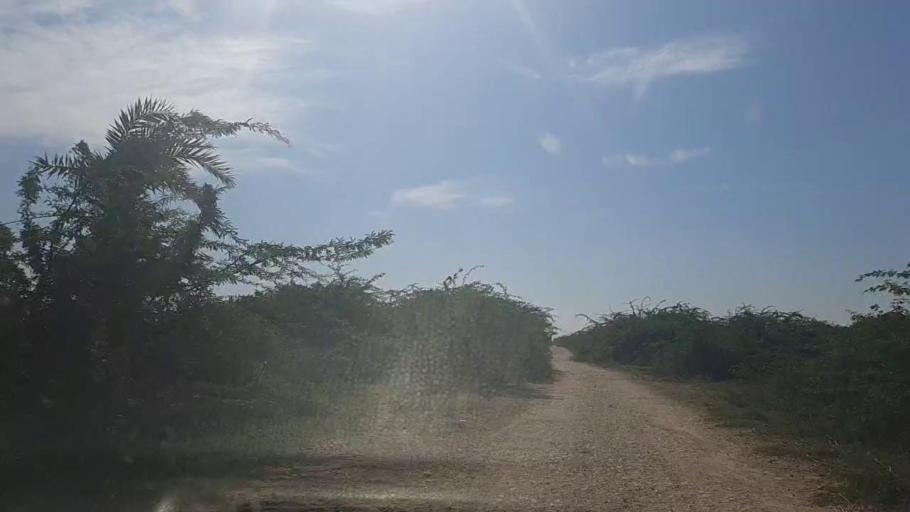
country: PK
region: Sindh
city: Mirpur Batoro
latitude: 24.6769
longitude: 68.1826
